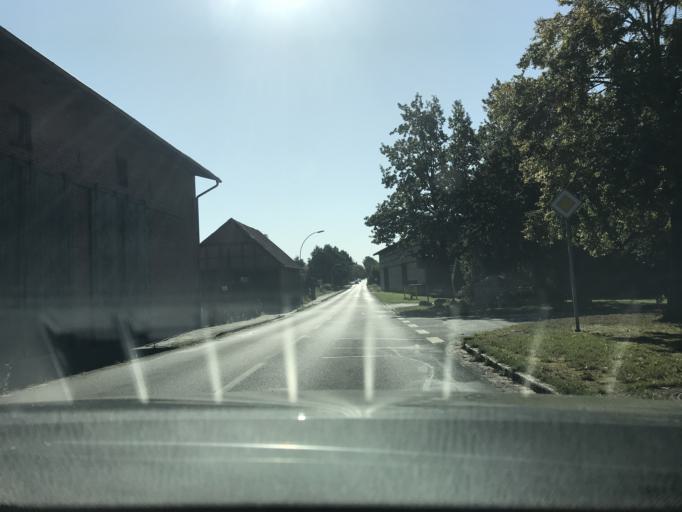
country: DE
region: Lower Saxony
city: Gerdau
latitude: 52.9217
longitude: 10.4141
